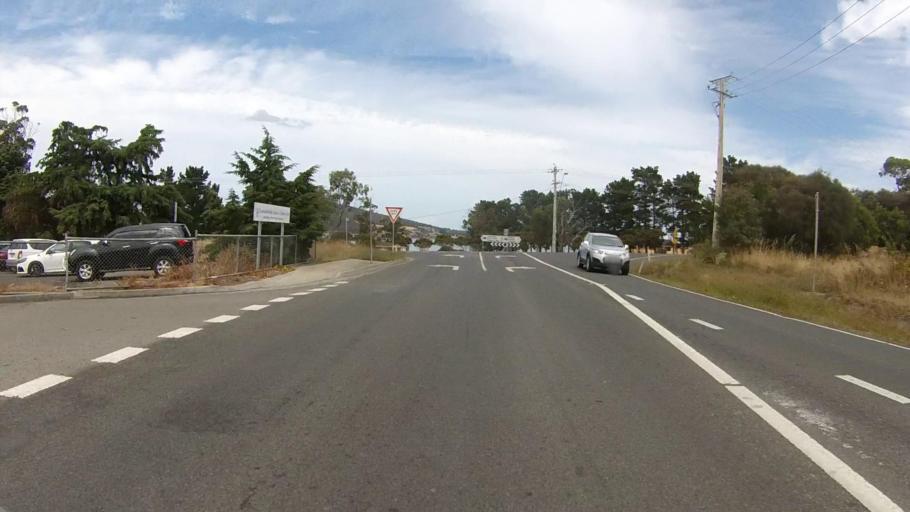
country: AU
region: Tasmania
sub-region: Clarence
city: Lauderdale
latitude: -42.9044
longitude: 147.4772
